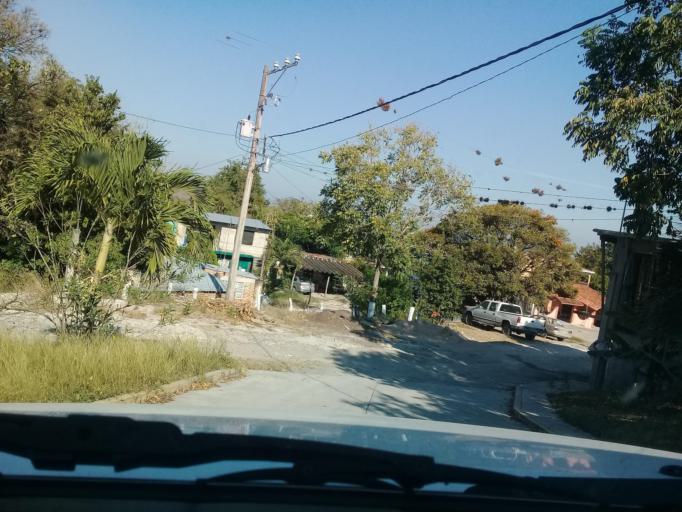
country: MX
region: Veracruz
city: Rinconada
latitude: 19.4023
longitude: -96.5581
